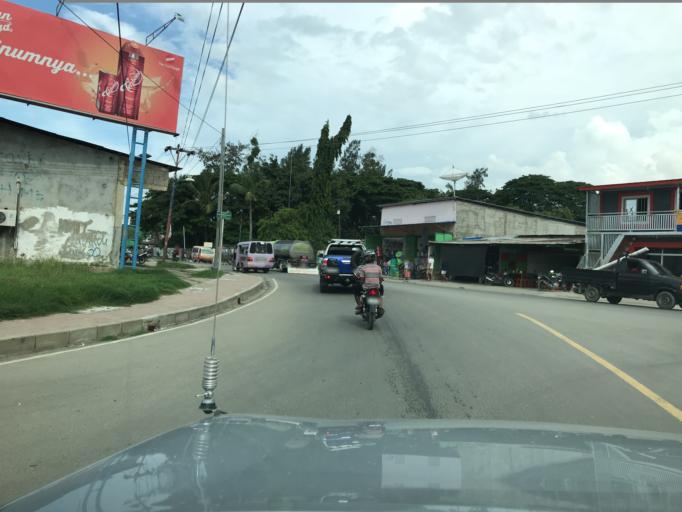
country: TL
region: Dili
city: Dili
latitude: -8.5609
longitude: 125.5616
